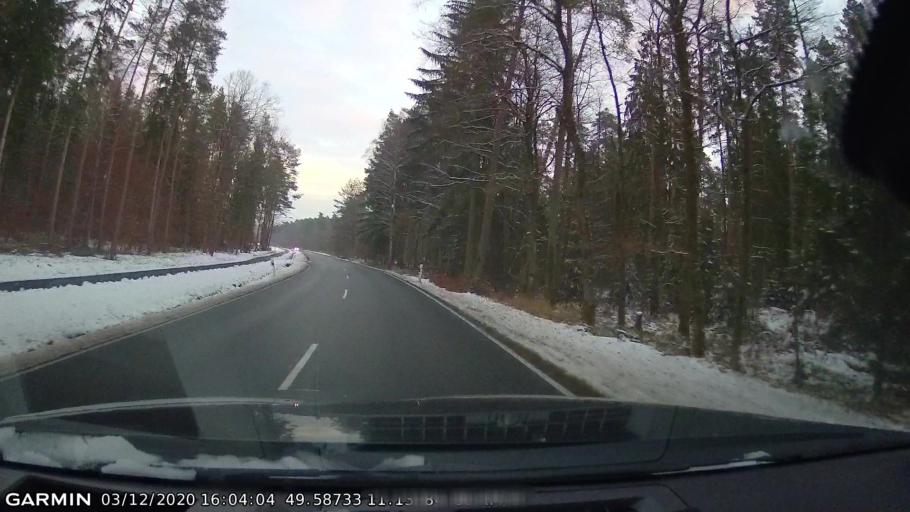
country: DE
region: Bavaria
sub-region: Upper Franconia
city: Dormitz
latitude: 49.5873
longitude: 11.1341
